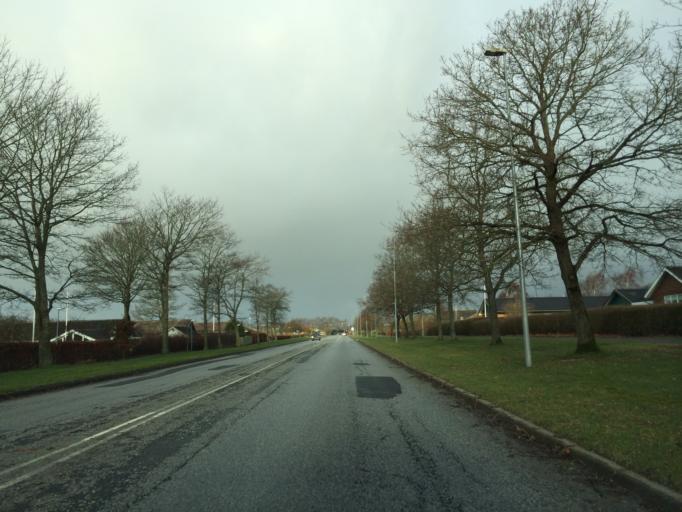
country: DK
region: Central Jutland
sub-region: Herning Kommune
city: Vildbjerg
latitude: 56.1906
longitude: 8.7630
